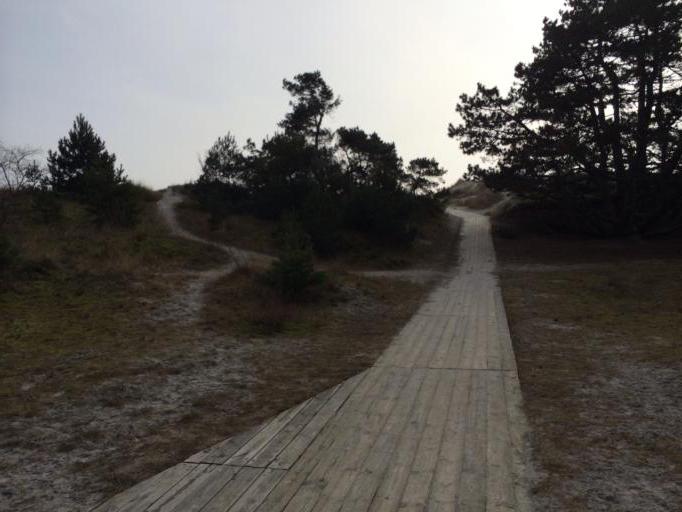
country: SE
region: Skane
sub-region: Vellinge Kommun
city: Skanor med Falsterbo
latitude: 55.3915
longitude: 12.8489
